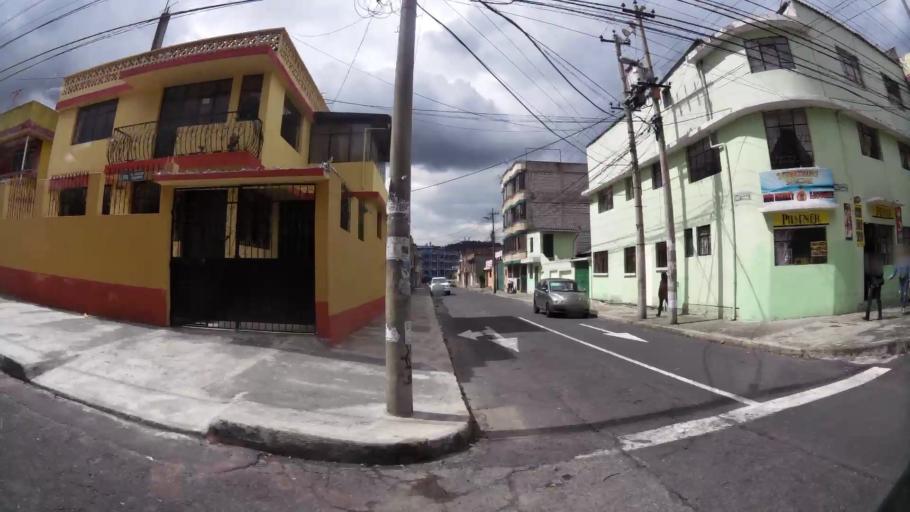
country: EC
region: Pichincha
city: Quito
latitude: -0.2474
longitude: -78.5319
